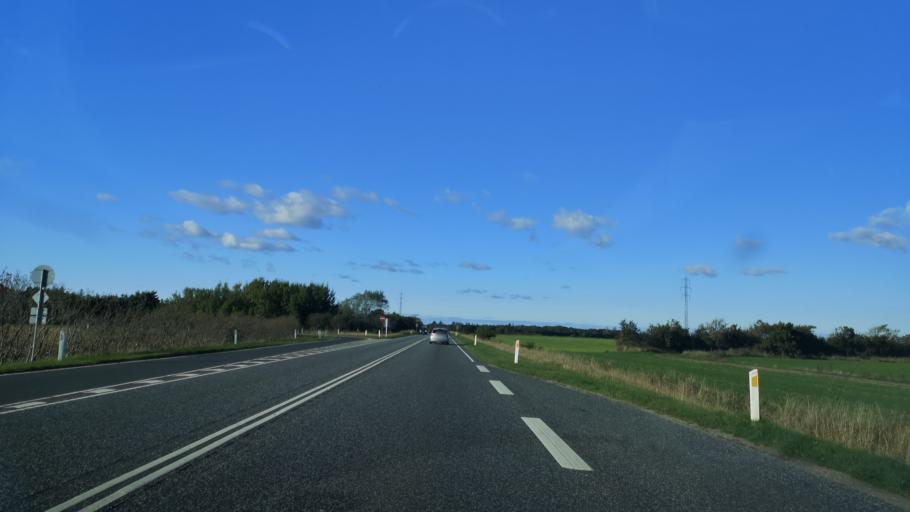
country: DK
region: South Denmark
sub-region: Esbjerg Kommune
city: Bramming
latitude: 55.4058
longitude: 8.7237
